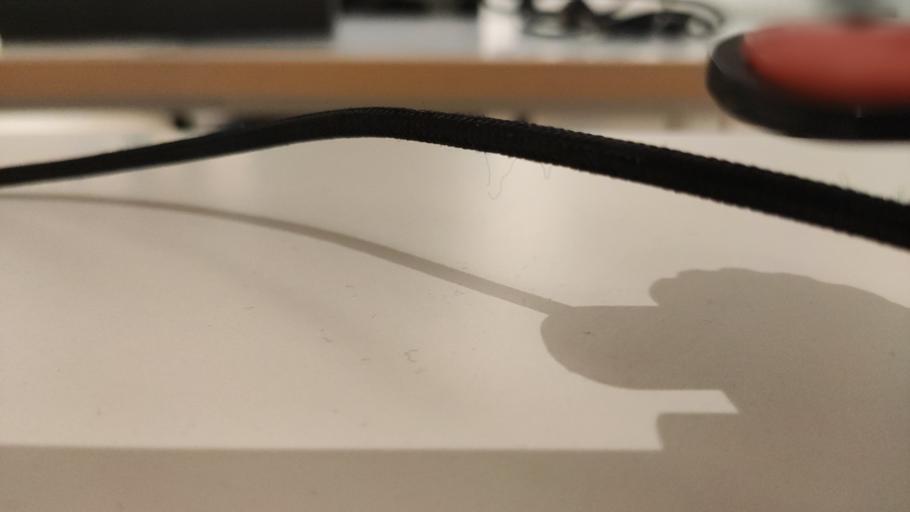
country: RU
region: Moskovskaya
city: Dorokhovo
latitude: 55.3790
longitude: 36.4032
